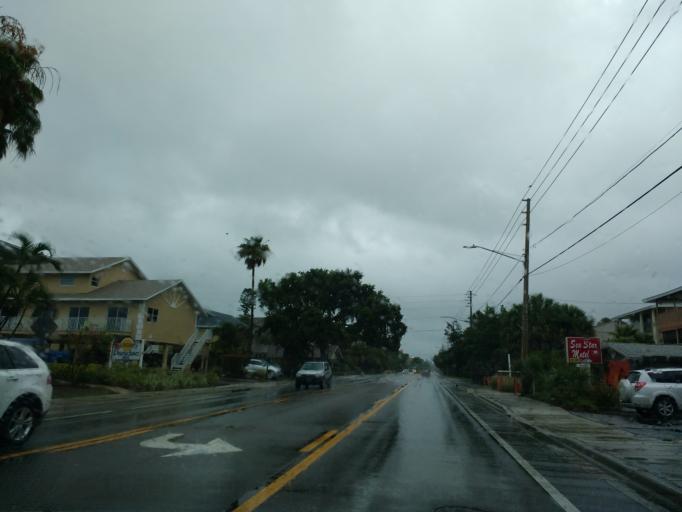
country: US
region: Florida
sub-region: Pinellas County
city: Harbor Bluffs
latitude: 27.9007
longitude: -82.8479
